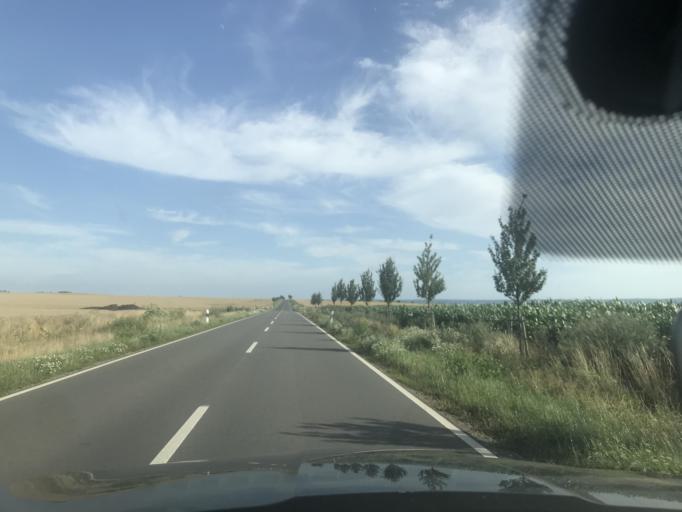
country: DE
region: Saxony-Anhalt
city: Wegeleben
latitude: 51.8618
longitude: 11.1853
